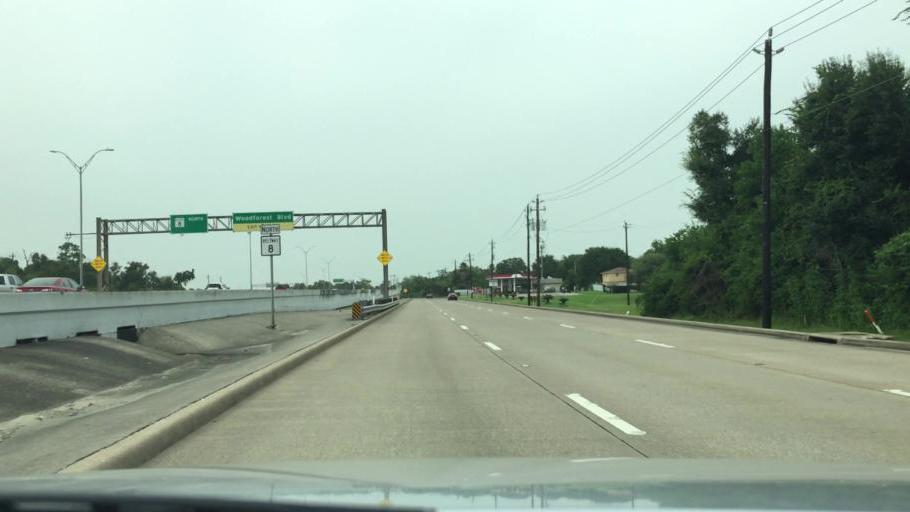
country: US
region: Texas
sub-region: Harris County
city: Cloverleaf
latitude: 29.7803
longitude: -95.1581
